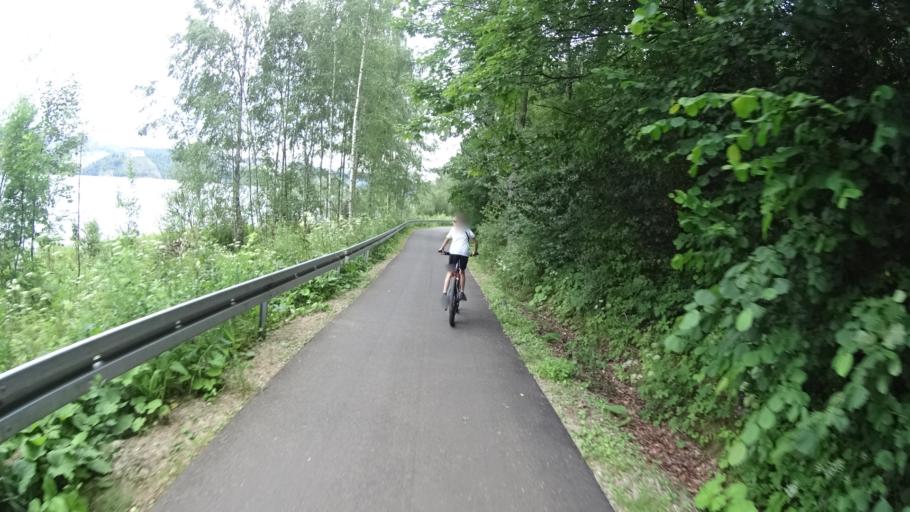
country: PL
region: Lesser Poland Voivodeship
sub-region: Powiat nowotarski
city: Niedzica
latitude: 49.4270
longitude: 20.3017
